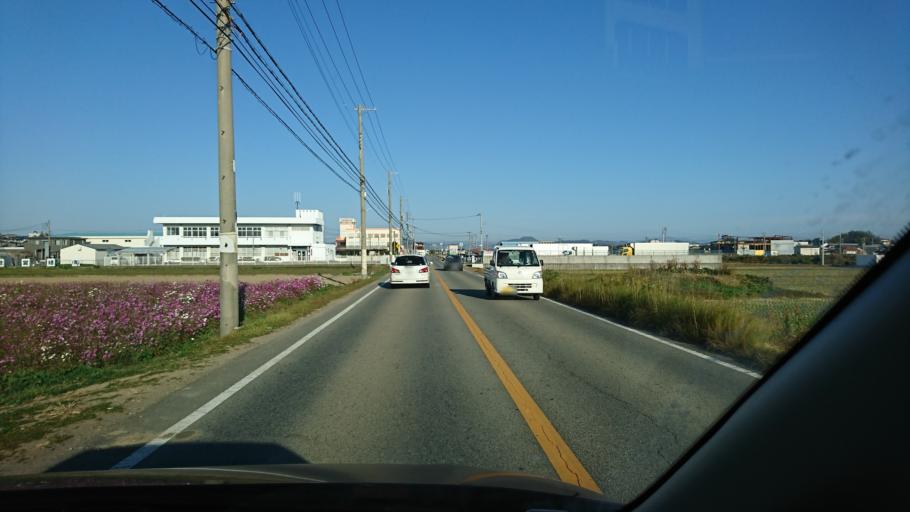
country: JP
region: Hyogo
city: Kakogawacho-honmachi
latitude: 34.7516
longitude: 134.8940
